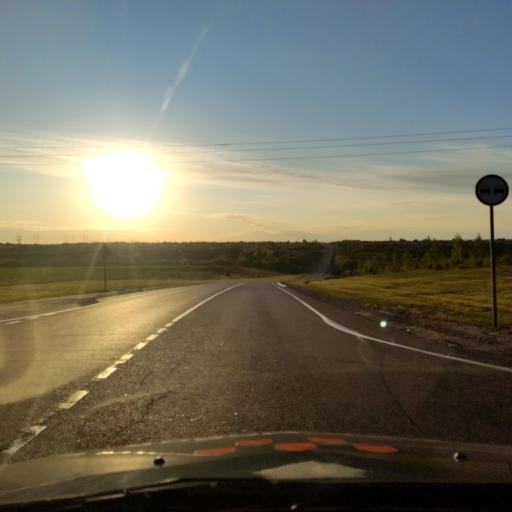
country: RU
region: Orjol
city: Livny
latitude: 52.4493
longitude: 37.6065
